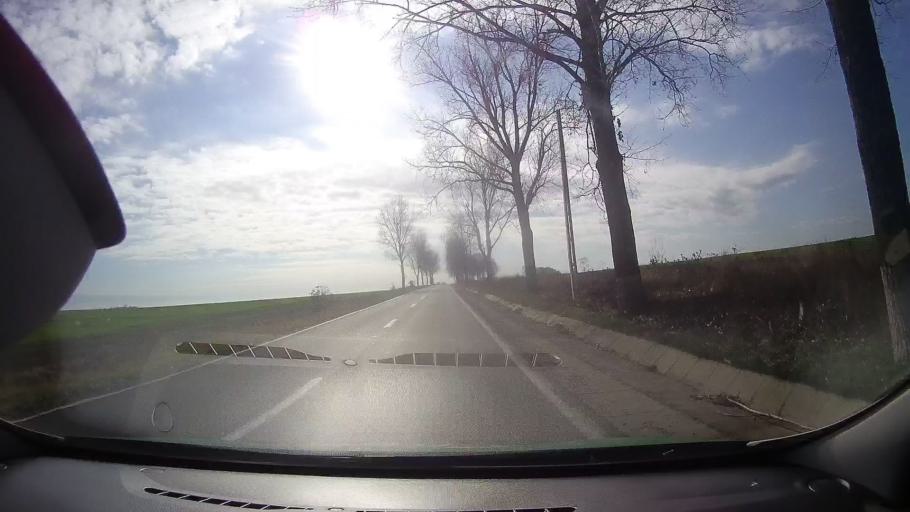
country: RO
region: Tulcea
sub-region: Comuna Valea Nucarilor
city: Agighiol
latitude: 44.9992
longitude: 28.8862
